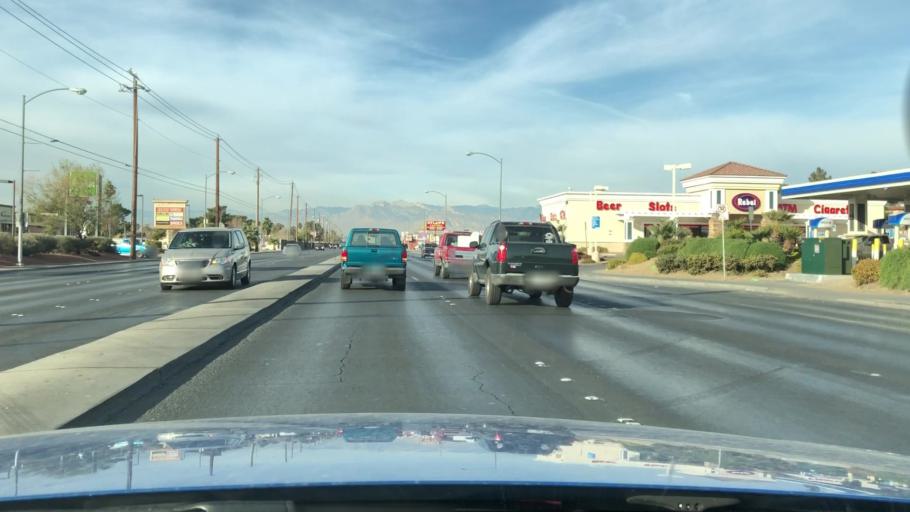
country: US
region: Nevada
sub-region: Clark County
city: North Las Vegas
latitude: 36.1959
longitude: -115.0990
